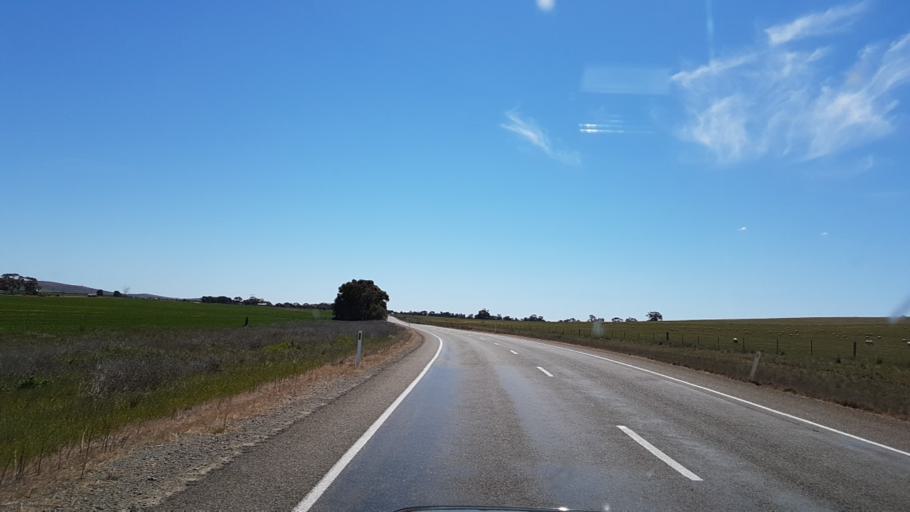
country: AU
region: South Australia
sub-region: Northern Areas
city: Jamestown
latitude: -33.4402
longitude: 138.8984
